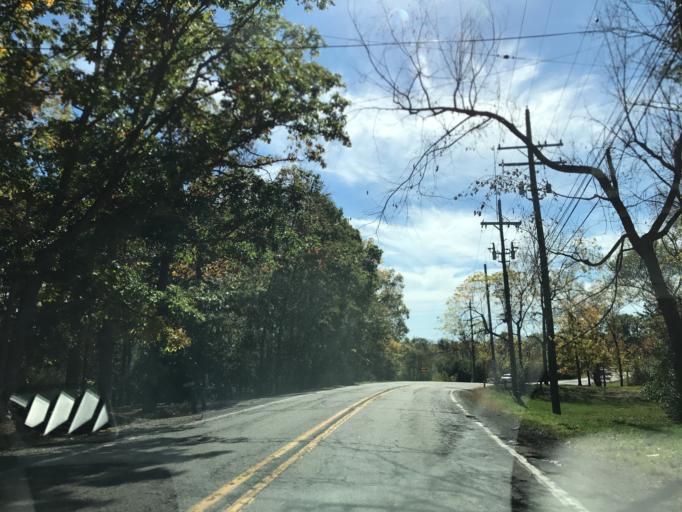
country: US
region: Michigan
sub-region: Washtenaw County
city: Ann Arbor
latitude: 42.2603
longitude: -83.6801
